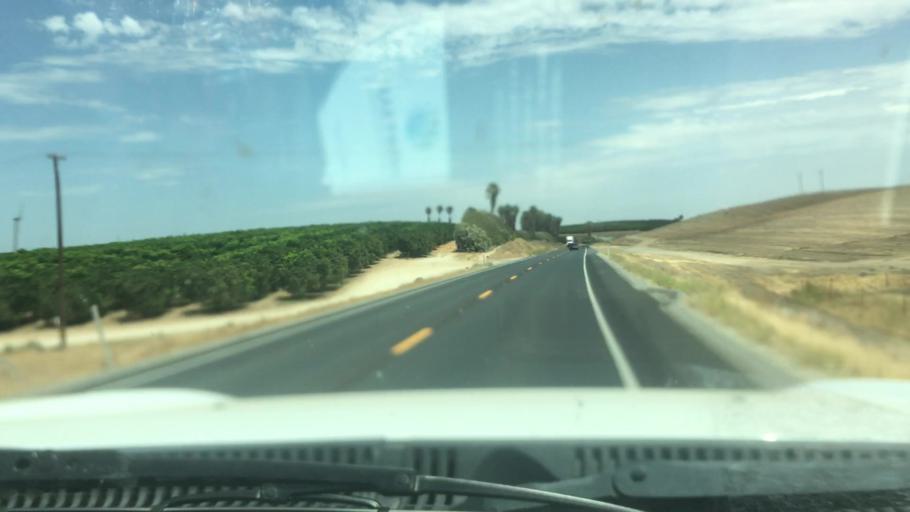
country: US
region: California
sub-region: Kern County
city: McFarland
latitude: 35.6309
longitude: -119.0852
